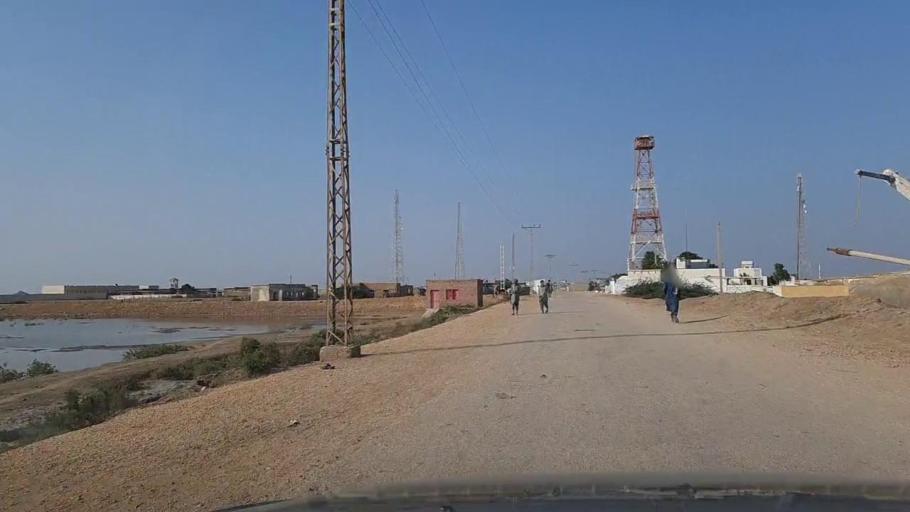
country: PK
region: Sindh
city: Keti Bandar
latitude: 24.1401
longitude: 67.4518
